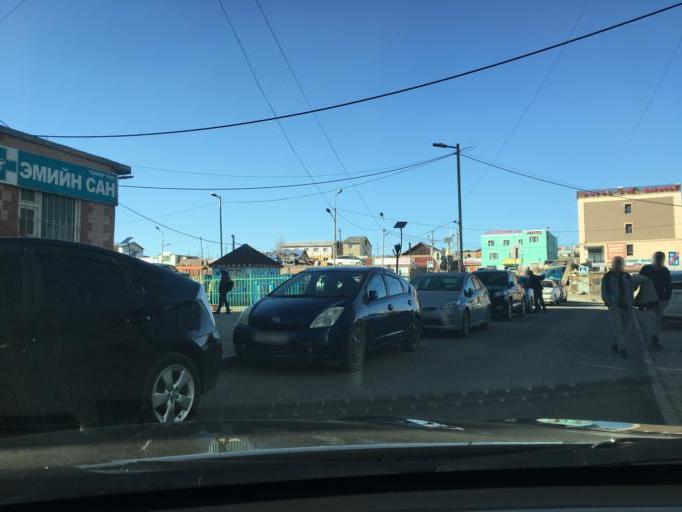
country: MN
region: Ulaanbaatar
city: Ulaanbaatar
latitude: 47.9247
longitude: 106.8742
